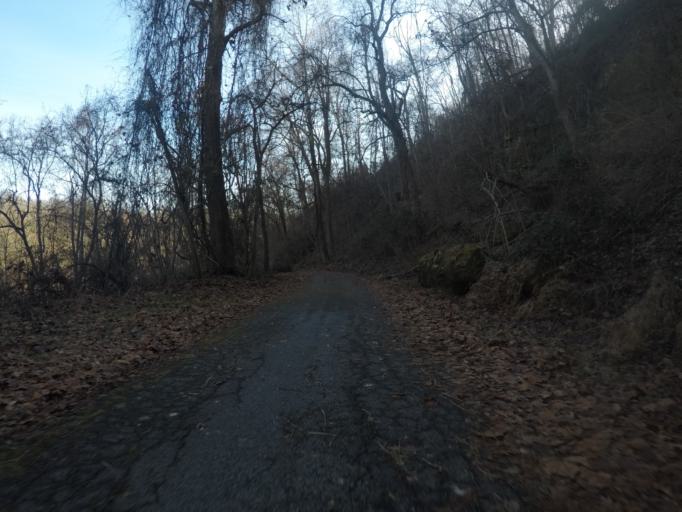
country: US
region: Ohio
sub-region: Lawrence County
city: Burlington
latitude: 38.3963
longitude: -82.5010
